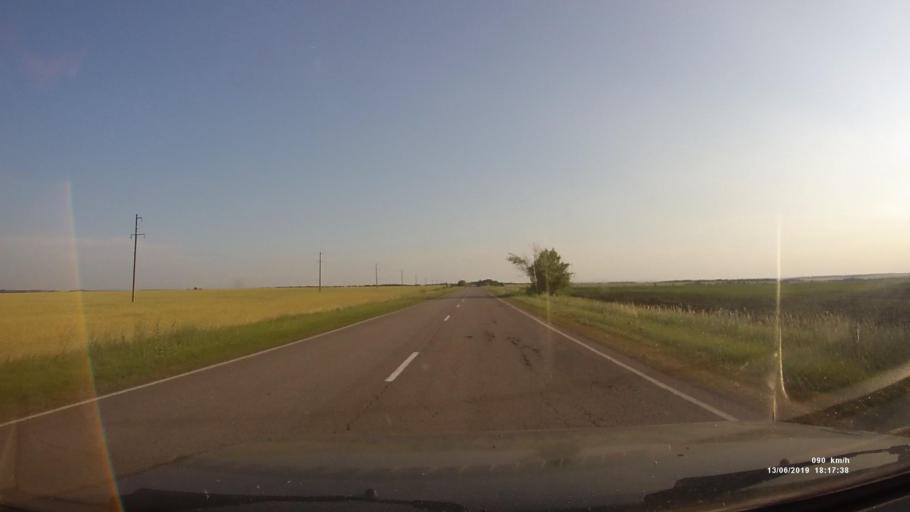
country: RU
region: Rostov
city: Kazanskaya
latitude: 49.9176
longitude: 41.3229
